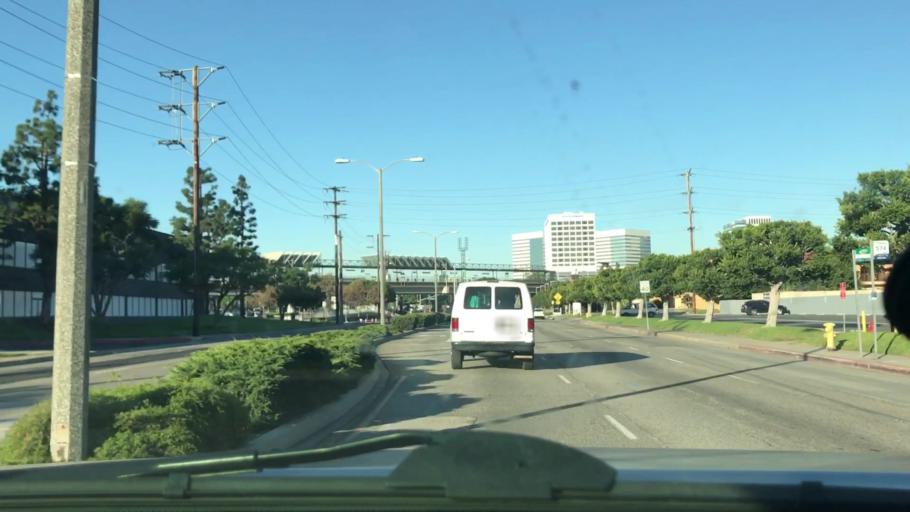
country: US
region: California
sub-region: Los Angeles County
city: Del Aire
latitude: 33.9164
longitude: -118.3841
